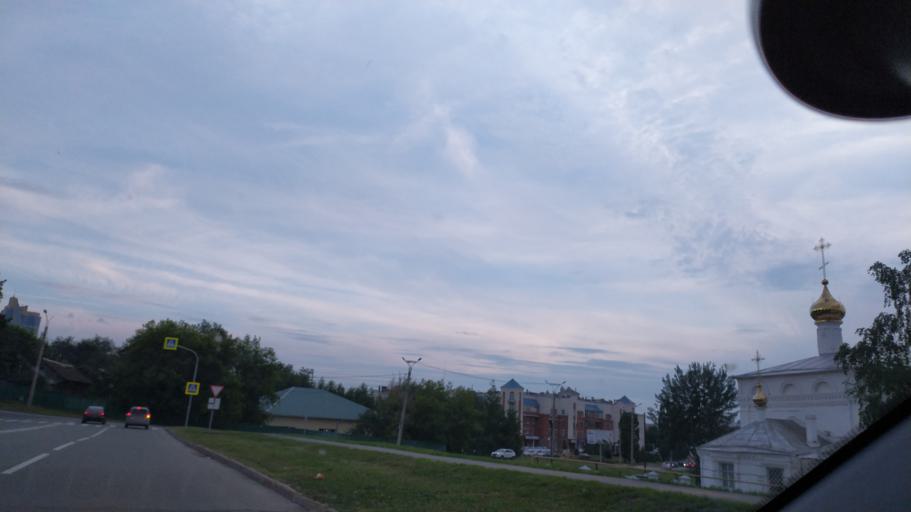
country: RU
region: Chuvashia
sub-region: Cheboksarskiy Rayon
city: Cheboksary
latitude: 56.1461
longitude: 47.2588
